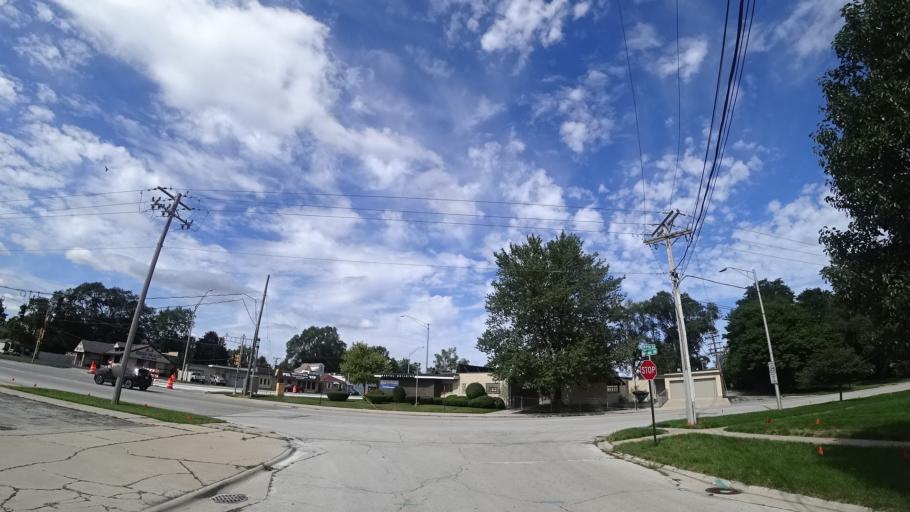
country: US
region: Illinois
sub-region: Cook County
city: Chicago Ridge
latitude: 41.7121
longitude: -87.7760
